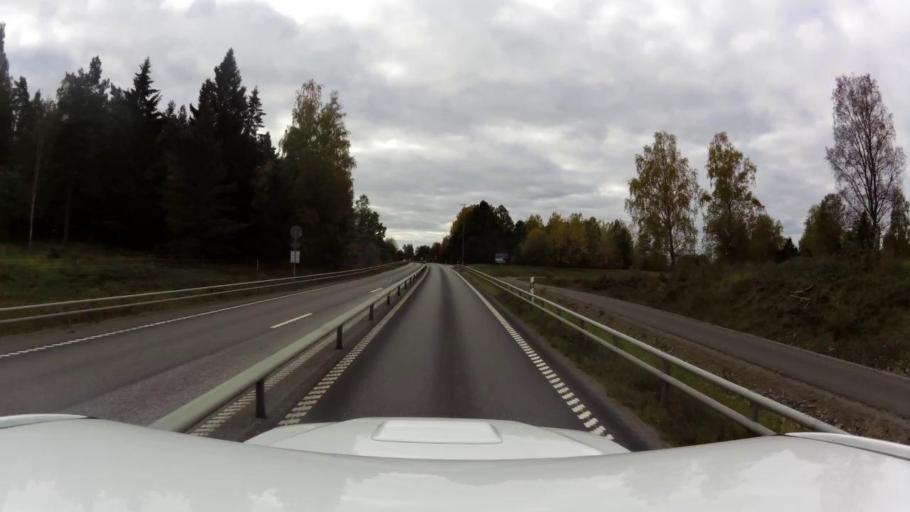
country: SE
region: OEstergoetland
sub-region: Linkopings Kommun
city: Malmslatt
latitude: 58.3039
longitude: 15.5643
